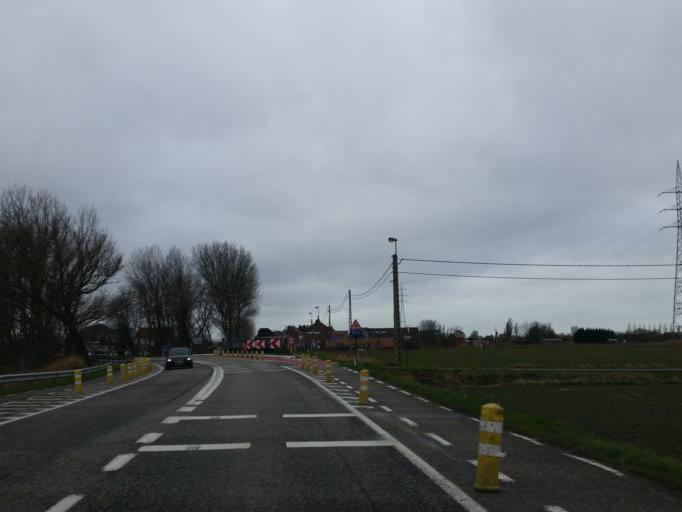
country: BE
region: Flanders
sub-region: Provincie West-Vlaanderen
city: Bredene
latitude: 51.2245
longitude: 2.9932
